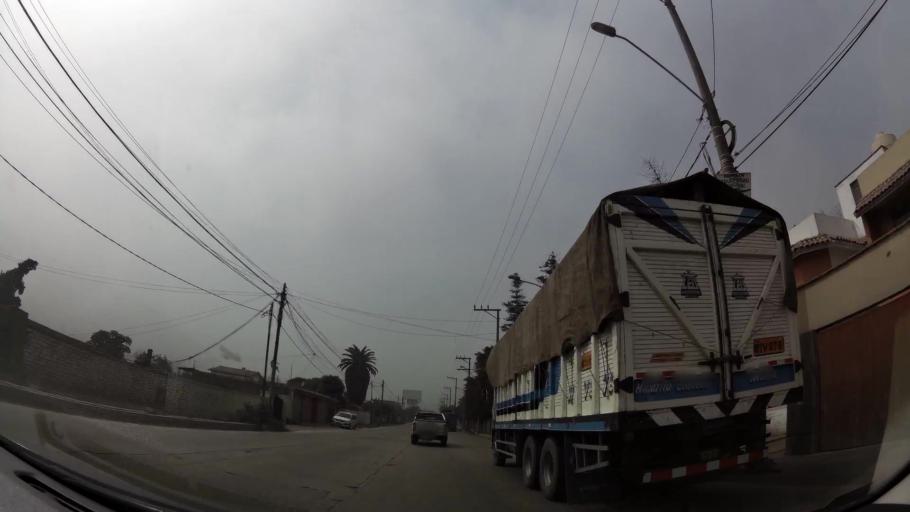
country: PE
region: Lima
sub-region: Lima
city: Chaclacayo
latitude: -11.9700
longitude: -76.7509
